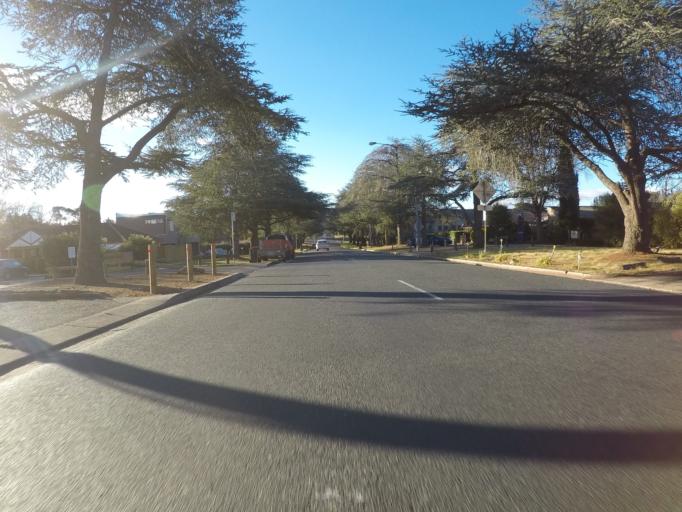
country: AU
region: Australian Capital Territory
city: Forrest
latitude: -35.3072
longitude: 149.0982
